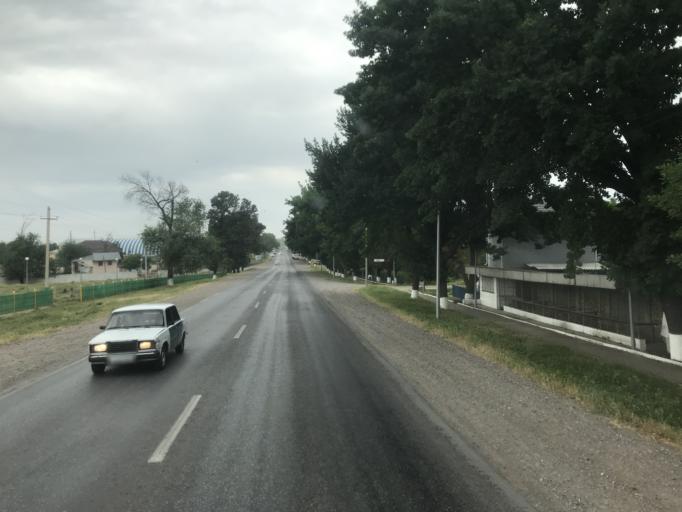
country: KZ
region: Ongtustik Qazaqstan
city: Saryaghash
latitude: 41.4910
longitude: 69.2808
